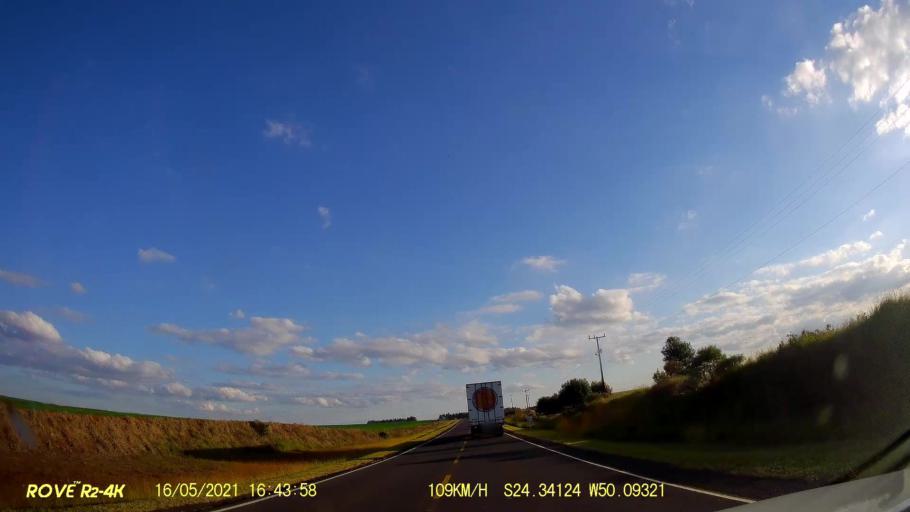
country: BR
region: Parana
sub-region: Pirai Do Sul
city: Pirai do Sul
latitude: -24.3414
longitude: -50.0934
